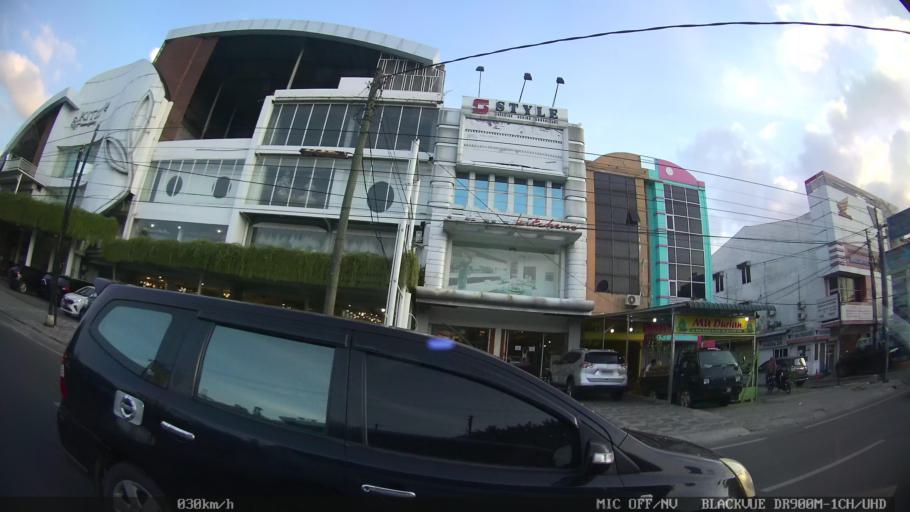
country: ID
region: North Sumatra
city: Medan
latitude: 3.5901
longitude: 98.6547
